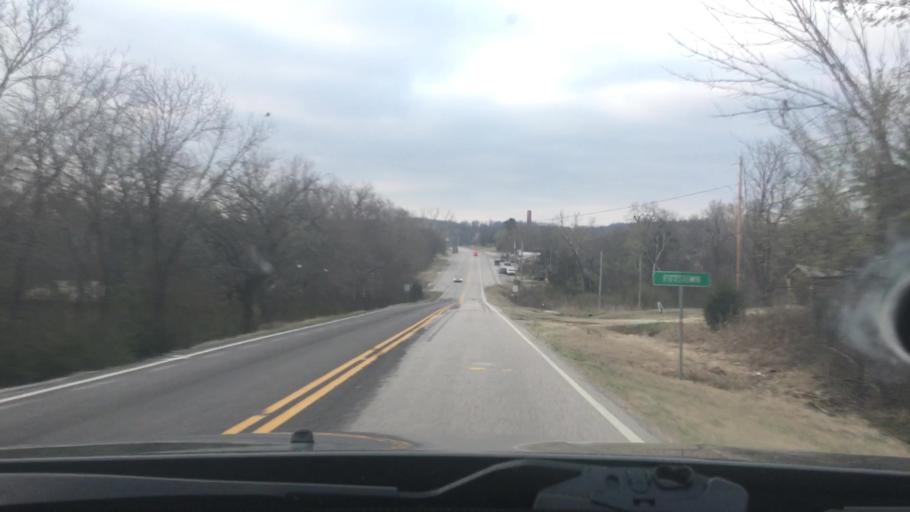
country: US
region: Oklahoma
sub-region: Pontotoc County
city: Ada
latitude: 34.6185
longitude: -96.6348
